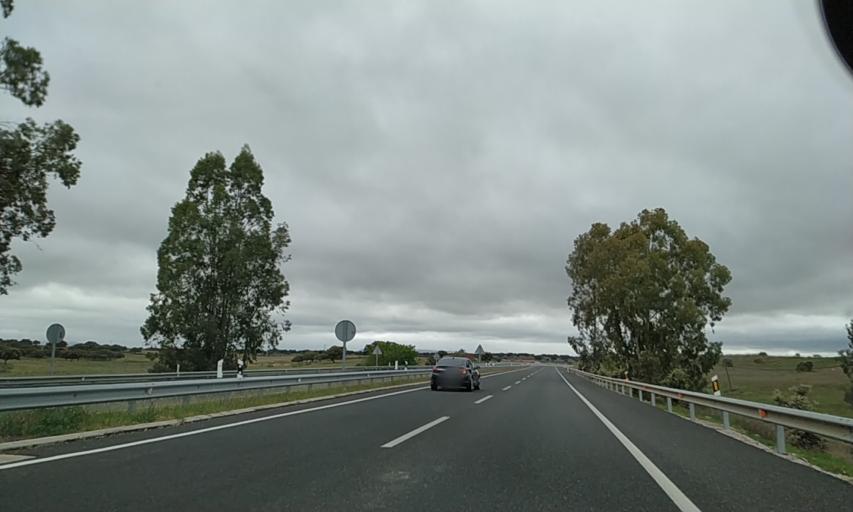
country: ES
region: Extremadura
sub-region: Provincia de Caceres
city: Caceres
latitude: 39.4646
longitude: -6.4098
